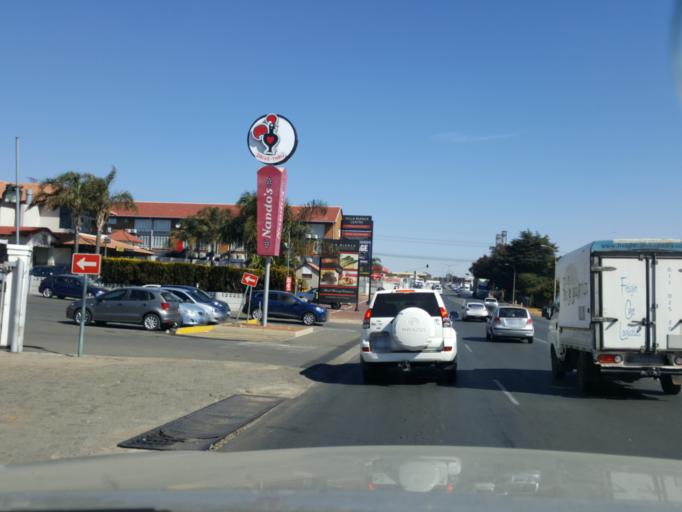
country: ZA
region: Gauteng
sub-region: City of Johannesburg Metropolitan Municipality
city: Modderfontein
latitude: -26.1342
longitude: 28.1968
